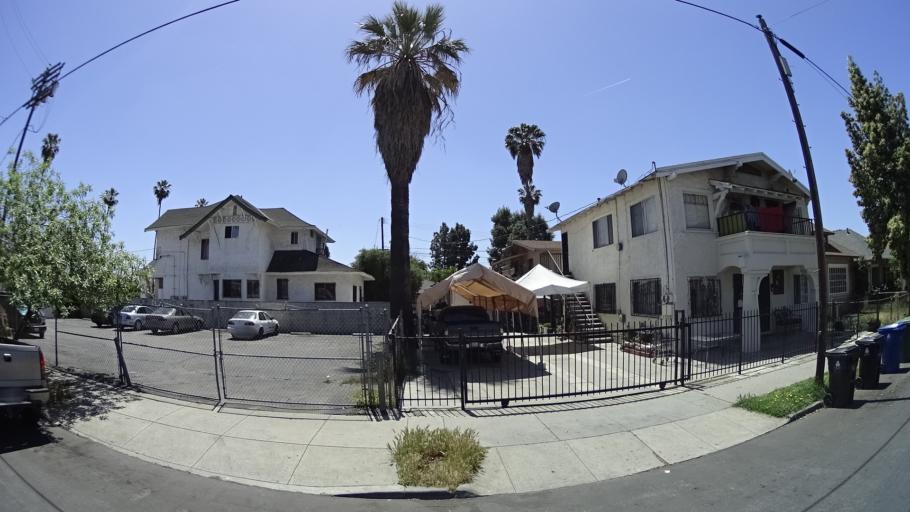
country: US
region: California
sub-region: Los Angeles County
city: Los Angeles
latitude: 34.0794
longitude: -118.2156
